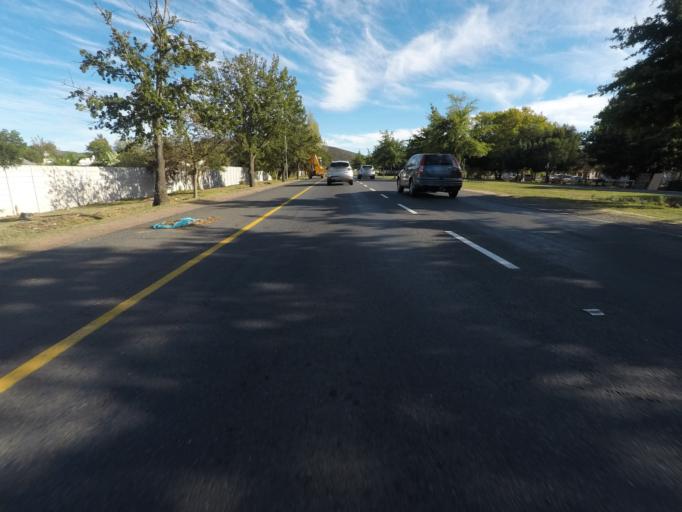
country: ZA
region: Western Cape
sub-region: Cape Winelands District Municipality
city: Stellenbosch
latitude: -33.9471
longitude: 18.8536
